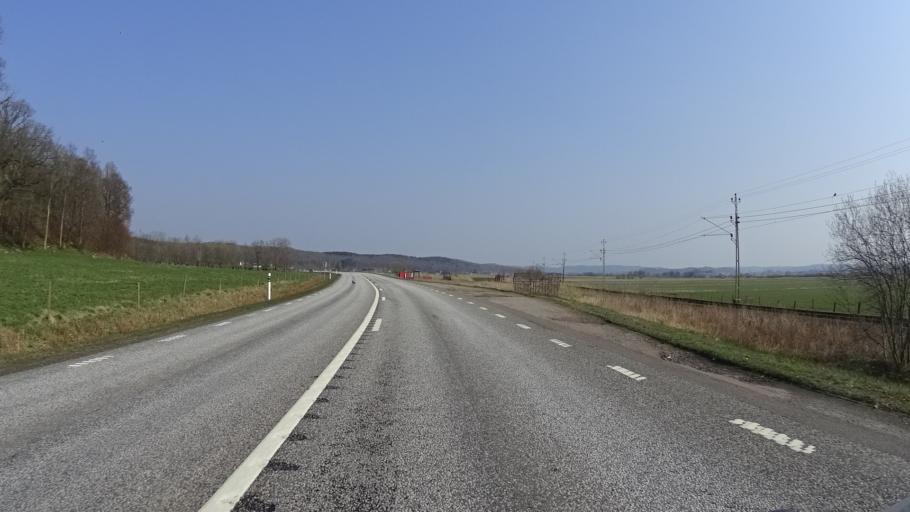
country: SE
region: Vaestra Goetaland
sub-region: Marks Kommun
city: Horred
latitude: 57.3300
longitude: 12.4451
